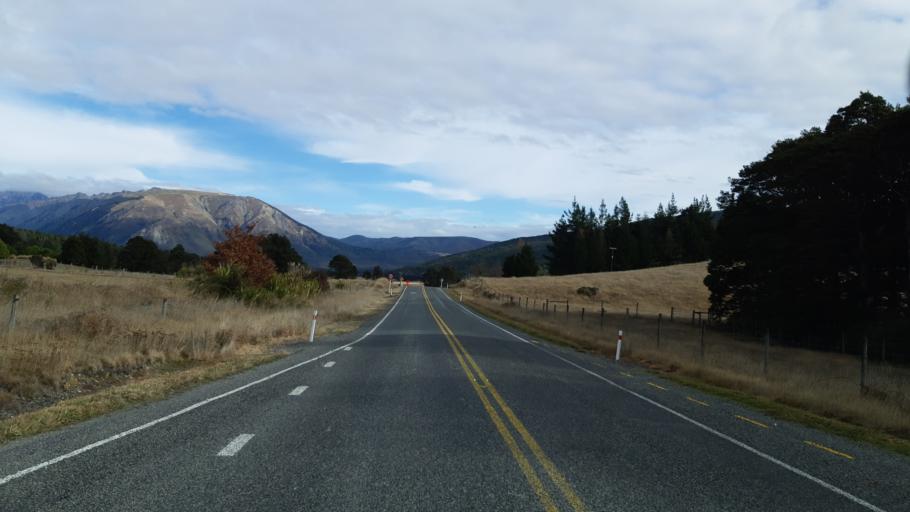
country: NZ
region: Tasman
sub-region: Tasman District
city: Wakefield
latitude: -41.7869
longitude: 172.8891
